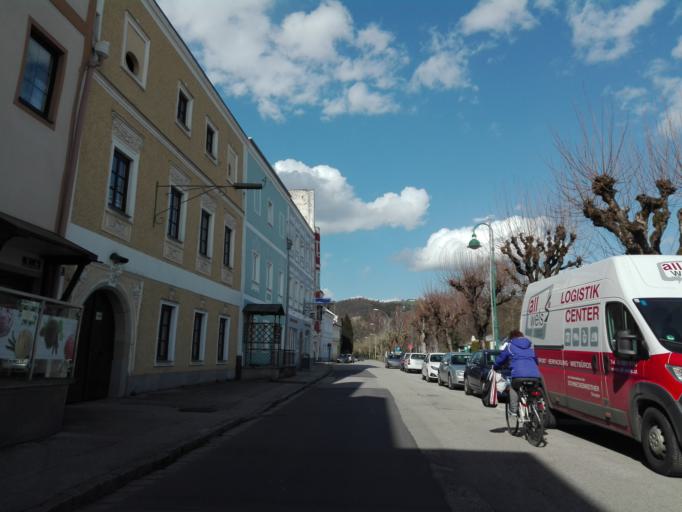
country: AT
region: Upper Austria
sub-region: Politischer Bezirk Urfahr-Umgebung
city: Feldkirchen an der Donau
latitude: 48.3689
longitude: 14.0264
